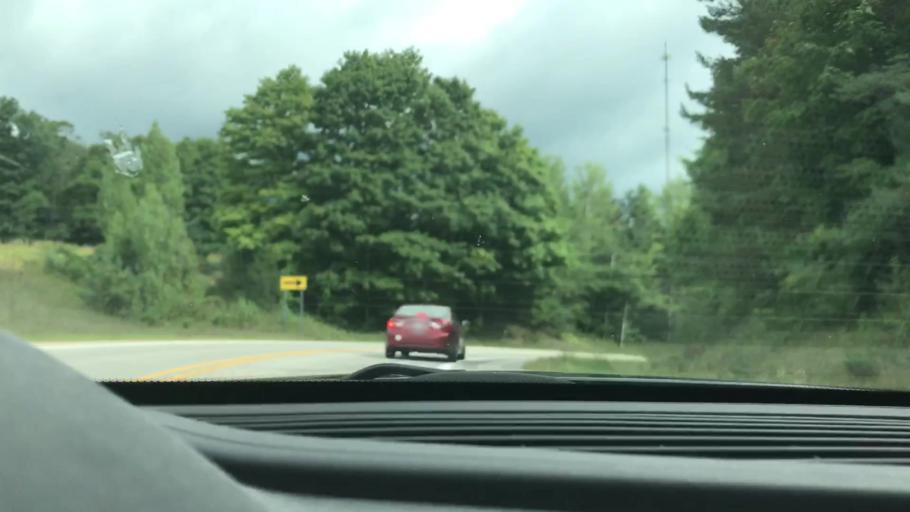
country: US
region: Michigan
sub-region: Antrim County
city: Bellaire
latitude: 45.0849
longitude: -85.2871
